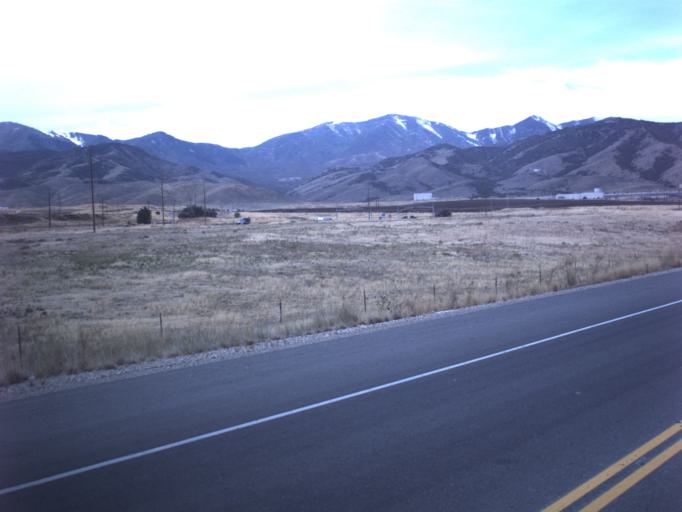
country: US
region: Utah
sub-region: Salt Lake County
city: Oquirrh
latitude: 40.6539
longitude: -112.0703
